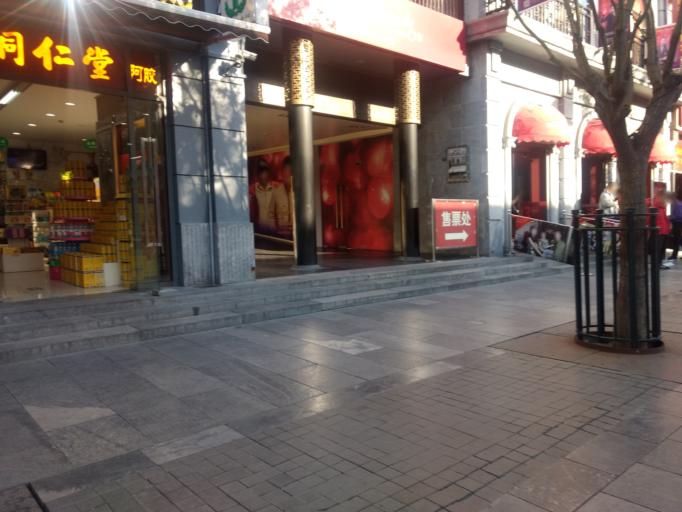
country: CN
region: Beijing
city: Beijing
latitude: 39.8960
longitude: 116.3919
